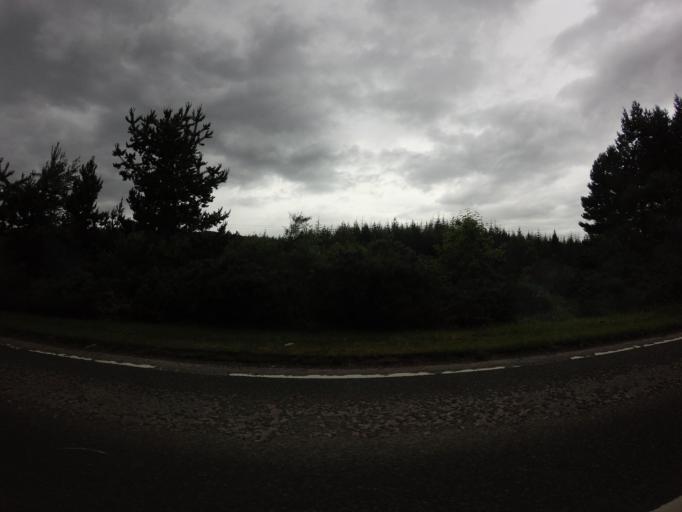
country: GB
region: Scotland
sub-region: Highland
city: Muir of Ord
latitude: 57.6347
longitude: -4.6798
